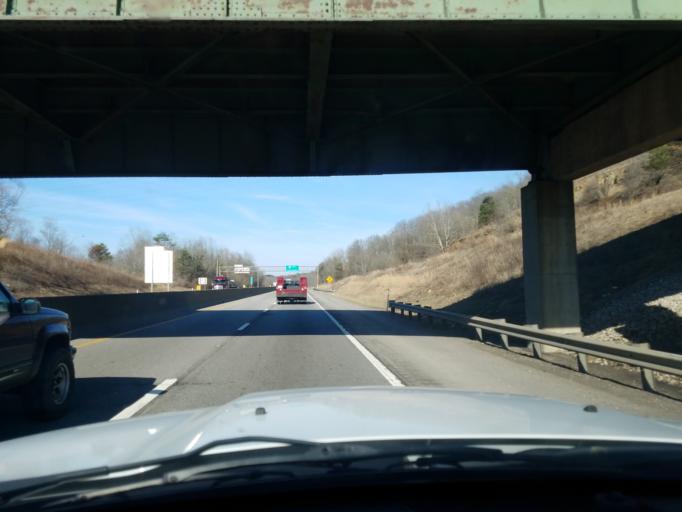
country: US
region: West Virginia
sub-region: Kanawha County
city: Nitro
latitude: 38.4481
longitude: -81.8489
